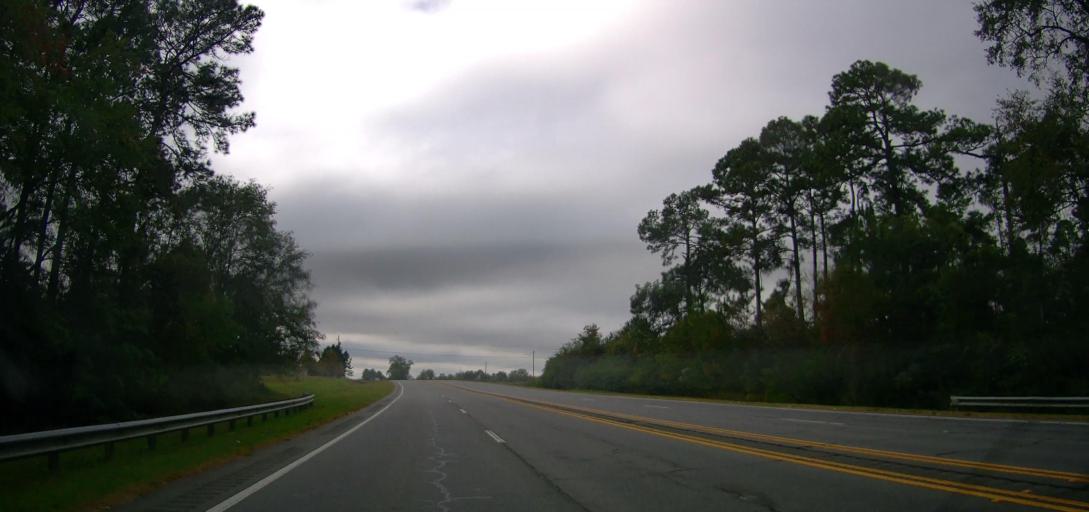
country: US
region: Georgia
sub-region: Colquitt County
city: Moultrie
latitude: 31.2580
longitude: -83.7051
